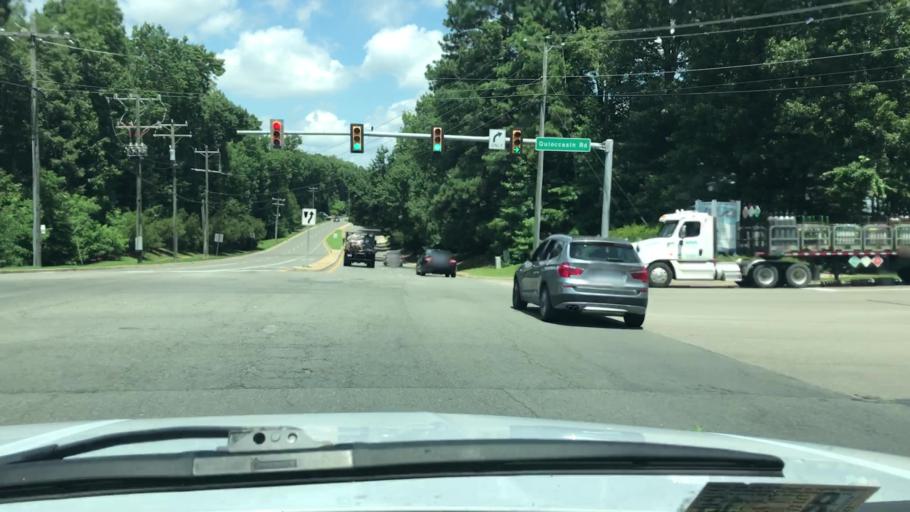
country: US
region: Virginia
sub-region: Henrico County
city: Tuckahoe
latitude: 37.6073
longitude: -77.5905
